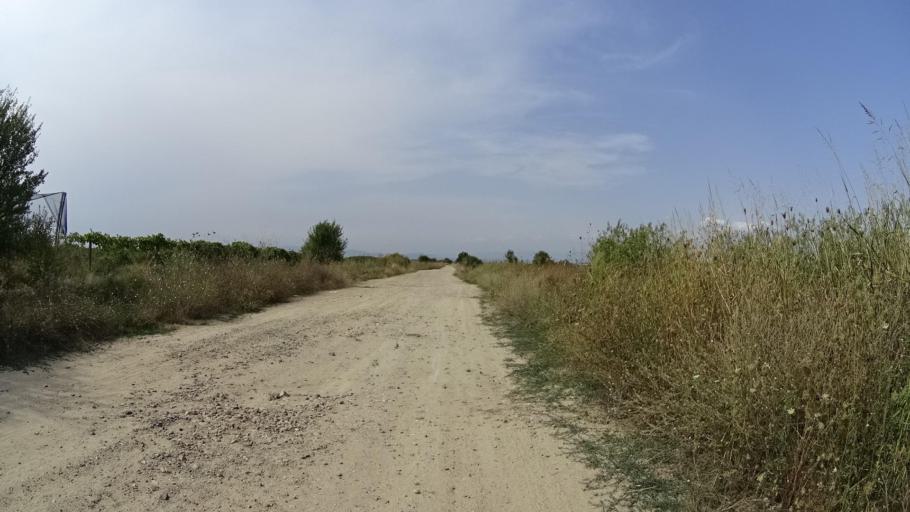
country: BG
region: Plovdiv
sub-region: Obshtina Kaloyanovo
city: Kaloyanovo
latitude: 42.2802
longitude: 24.7991
